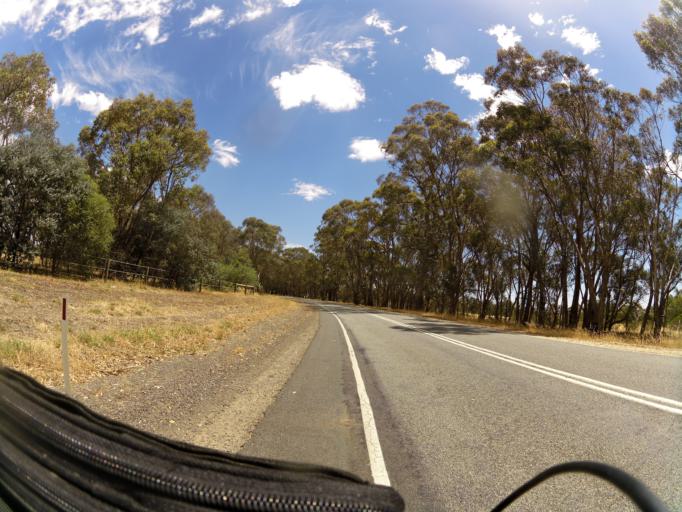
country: AU
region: Victoria
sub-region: Campaspe
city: Kyabram
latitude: -36.7849
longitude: 145.0944
